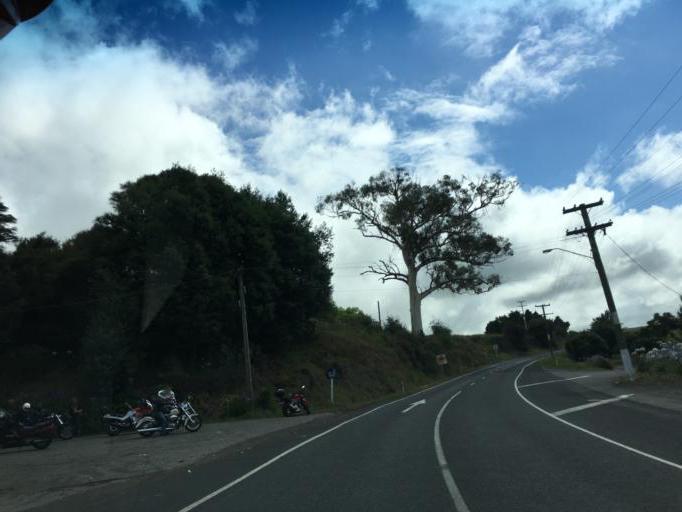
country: NZ
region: Hawke's Bay
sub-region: Napier City
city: Napier
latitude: -39.1331
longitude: 177.0040
